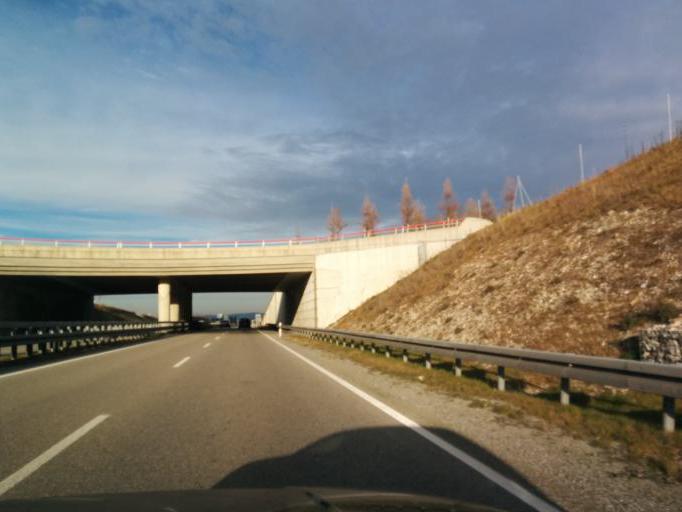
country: DE
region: Bavaria
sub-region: Swabia
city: Waltenhofen
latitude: 47.6287
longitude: 10.2792
